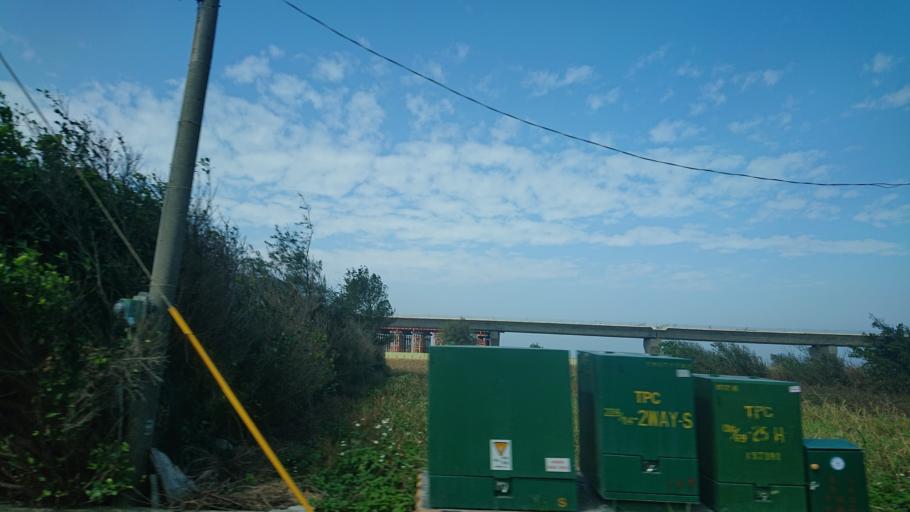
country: TW
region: Taiwan
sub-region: Changhua
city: Chang-hua
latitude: 23.9146
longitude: 120.3116
